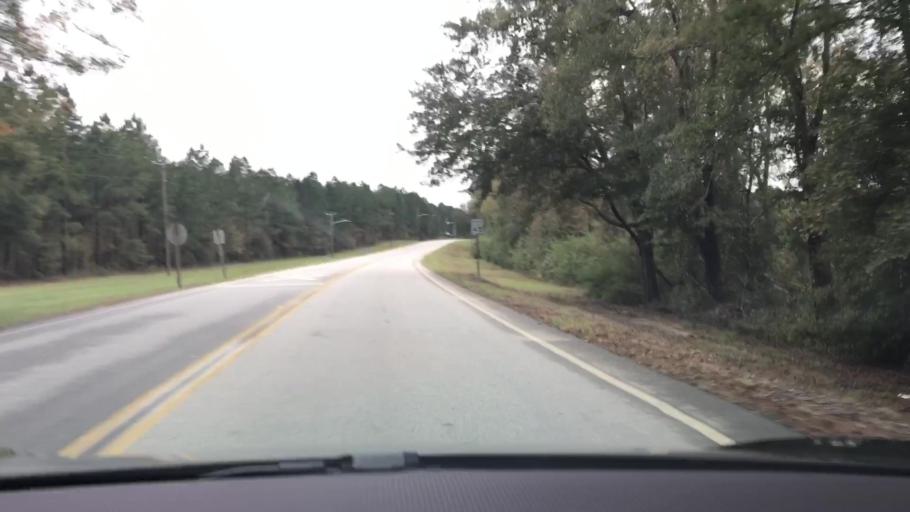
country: US
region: Georgia
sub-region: Jefferson County
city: Wrens
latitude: 33.2230
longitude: -82.4628
